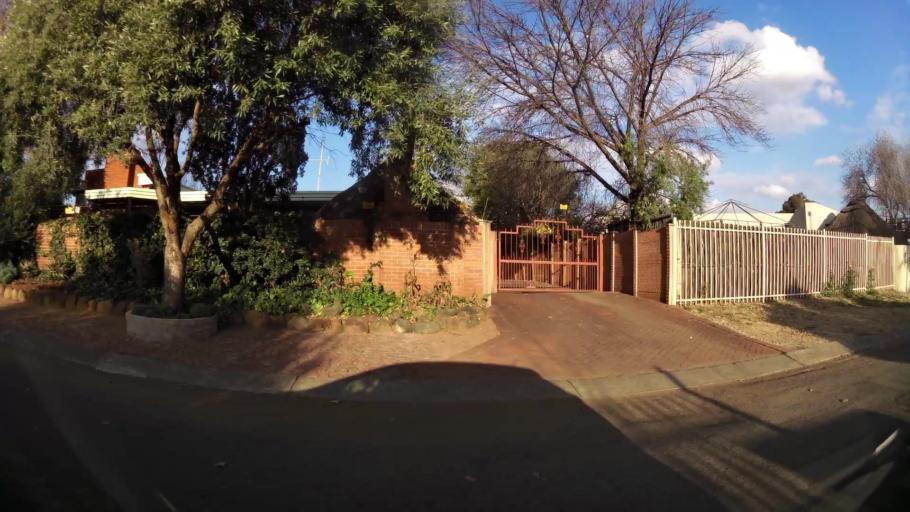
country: ZA
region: Orange Free State
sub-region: Mangaung Metropolitan Municipality
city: Bloemfontein
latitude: -29.1492
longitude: 26.1896
